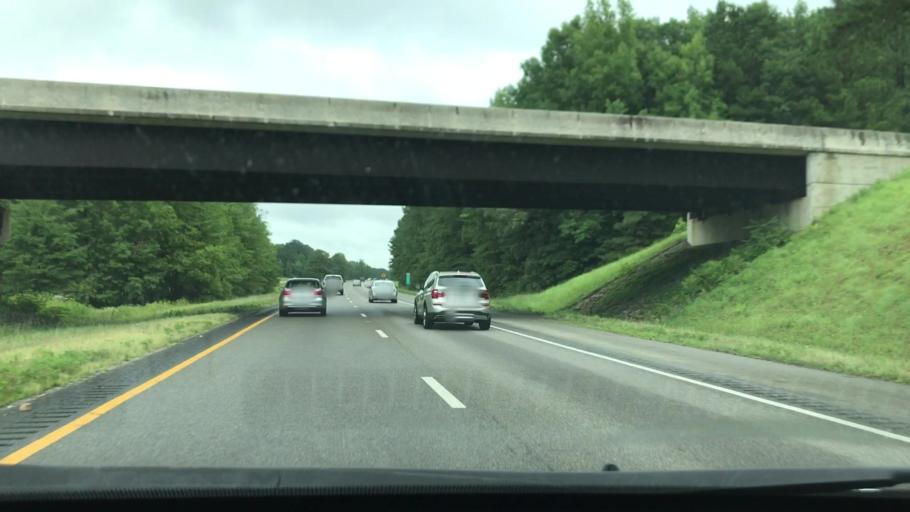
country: US
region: Virginia
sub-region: Sussex County
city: Sussex
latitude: 37.0342
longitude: -77.3900
